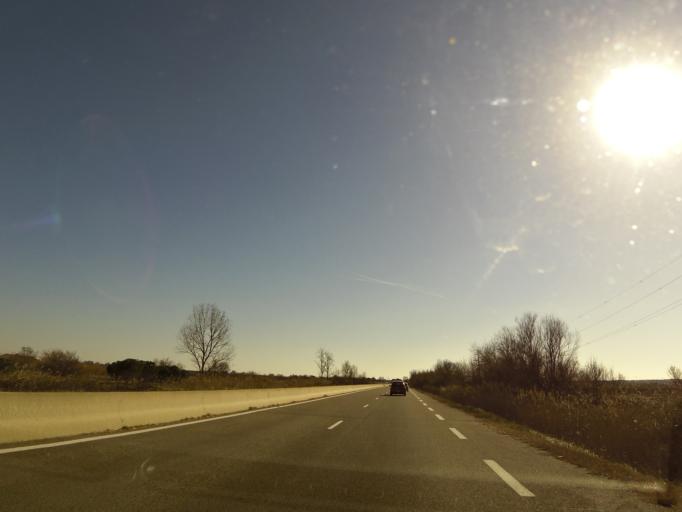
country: FR
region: Languedoc-Roussillon
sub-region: Departement du Gard
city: Aigues-Mortes
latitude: 43.6060
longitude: 4.1937
